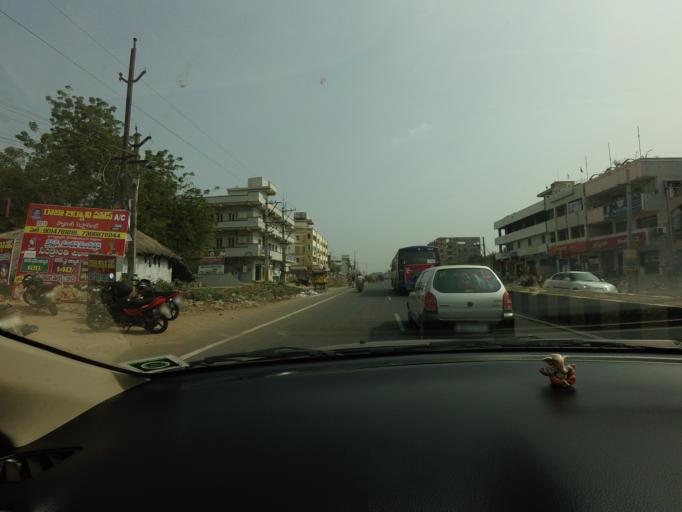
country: IN
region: Andhra Pradesh
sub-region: Krishna
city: Yanamalakuduru
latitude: 16.4835
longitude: 80.6870
